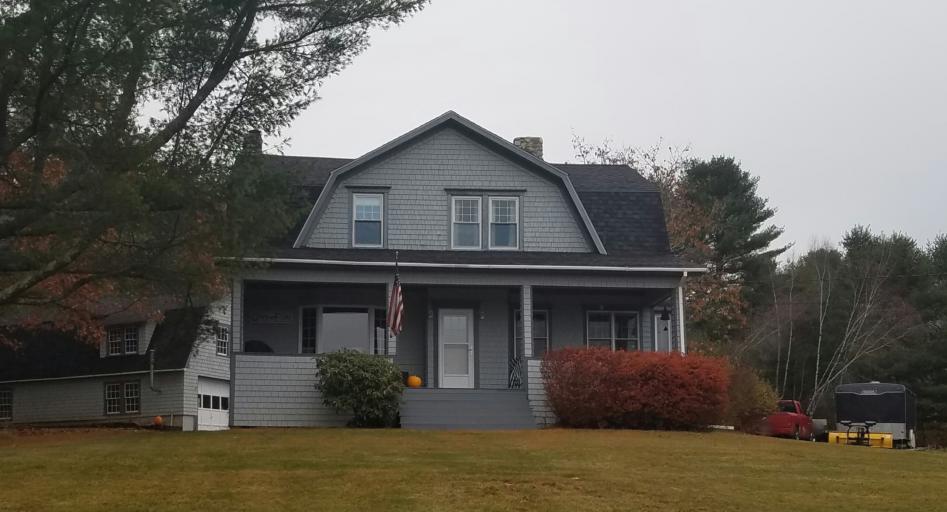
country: US
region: Maine
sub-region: Waldo County
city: Belfast
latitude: 44.4316
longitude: -68.9869
